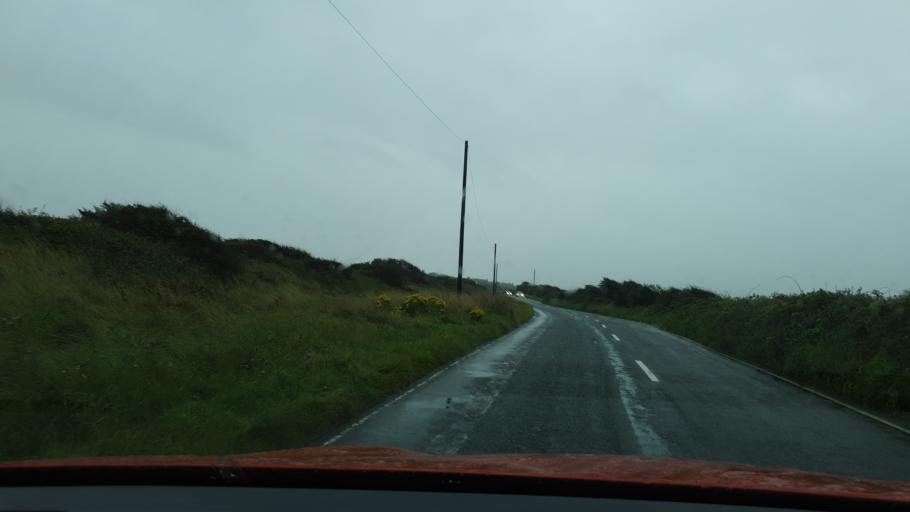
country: GB
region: England
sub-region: Cumbria
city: Barrow in Furness
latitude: 54.0893
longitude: -3.2441
